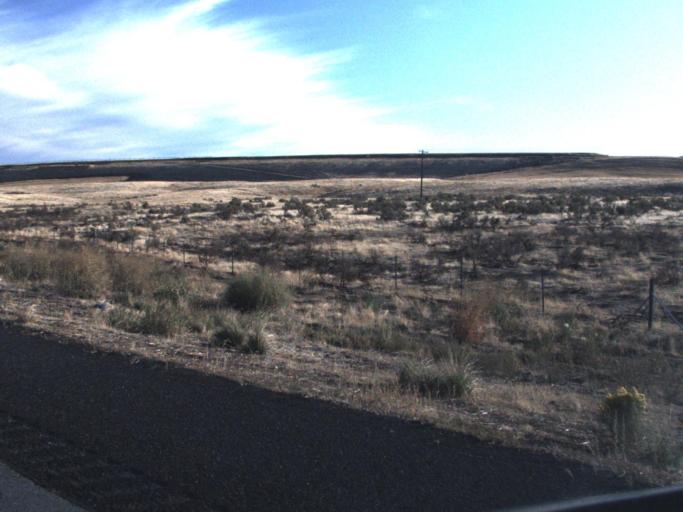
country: US
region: Washington
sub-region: Franklin County
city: Basin City
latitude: 46.5117
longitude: -119.0120
